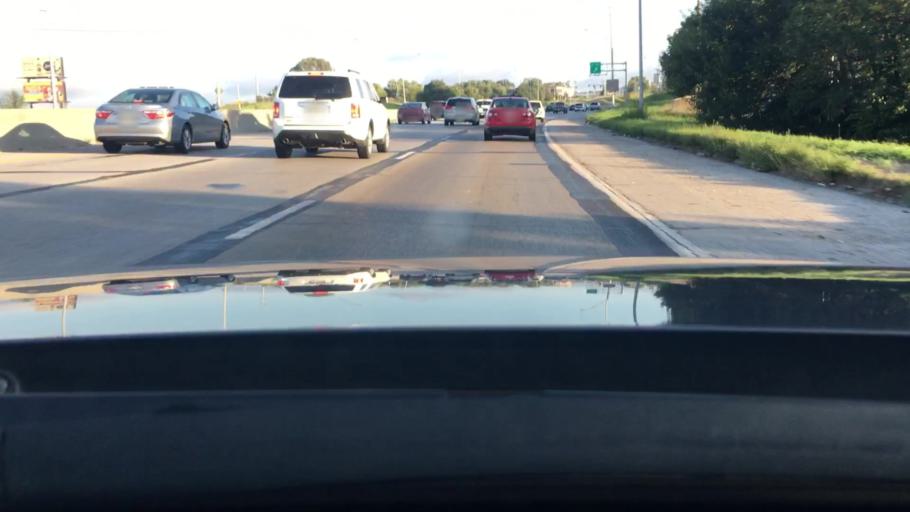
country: US
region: Nebraska
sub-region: Douglas County
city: Omaha
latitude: 41.2156
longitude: -95.9529
